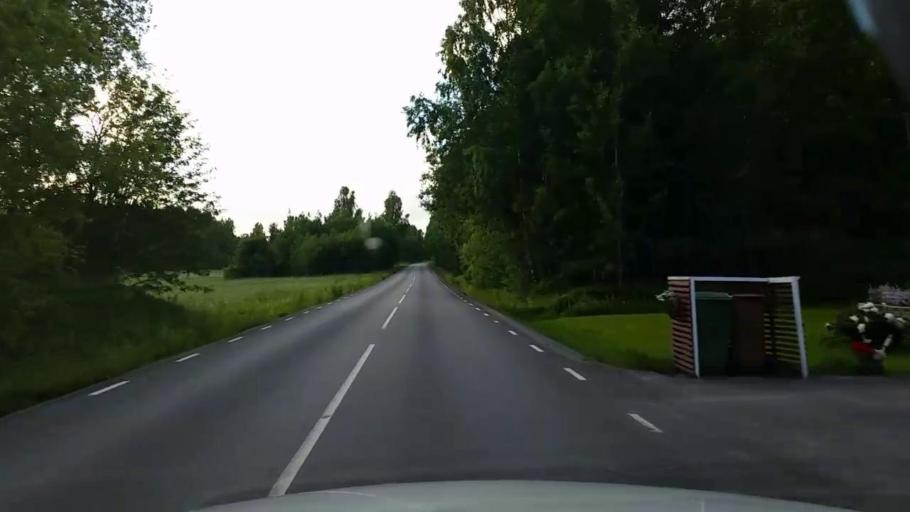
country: SE
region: Vaestmanland
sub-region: Kopings Kommun
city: Kolsva
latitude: 59.6253
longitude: 15.8214
